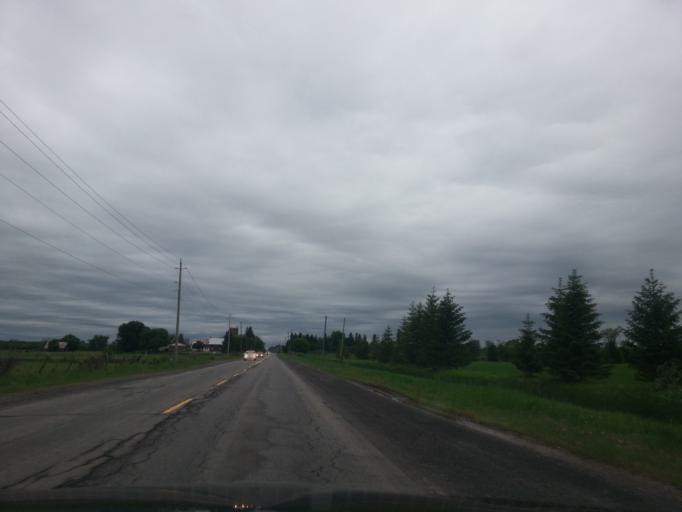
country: CA
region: Ontario
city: Bells Corners
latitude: 45.2353
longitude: -75.8768
